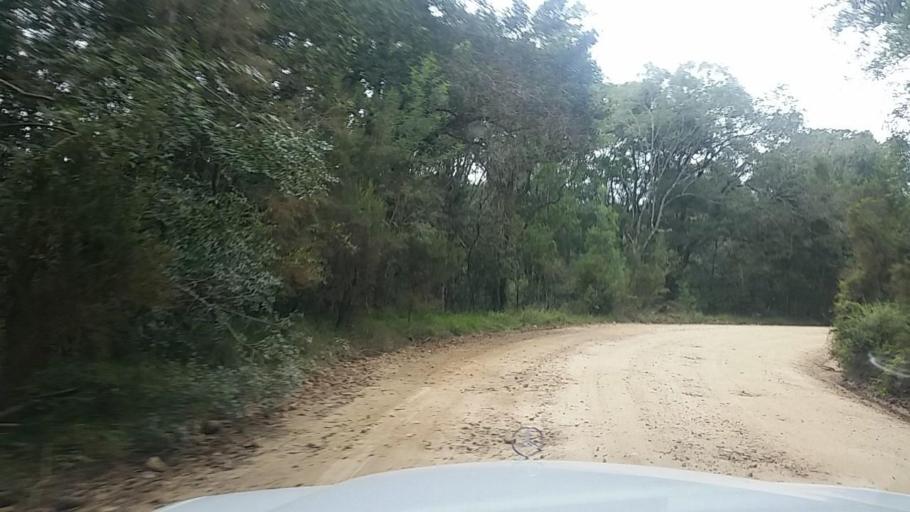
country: ZA
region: Western Cape
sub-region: Eden District Municipality
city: Knysna
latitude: -33.9412
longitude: 23.1617
